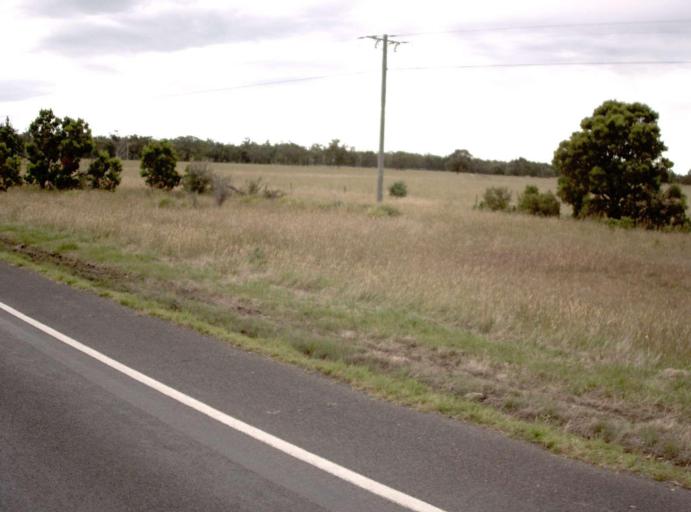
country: AU
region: Victoria
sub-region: Wellington
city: Sale
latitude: -38.2837
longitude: 147.0375
